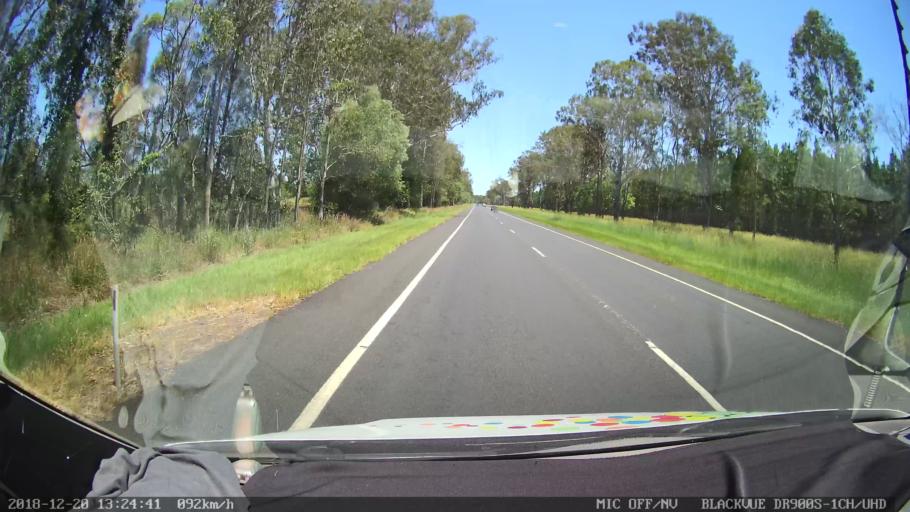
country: AU
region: New South Wales
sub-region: Richmond Valley
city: Casino
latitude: -29.1208
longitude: 152.9993
